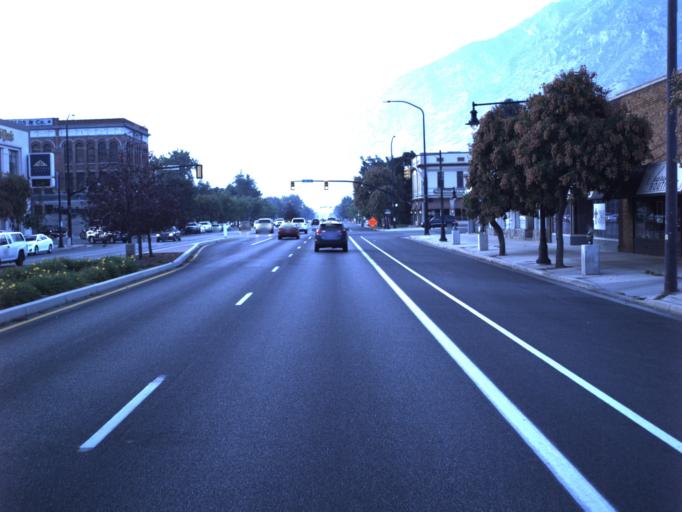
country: US
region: Utah
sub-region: Utah County
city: Springville
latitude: 40.1629
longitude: -111.6106
